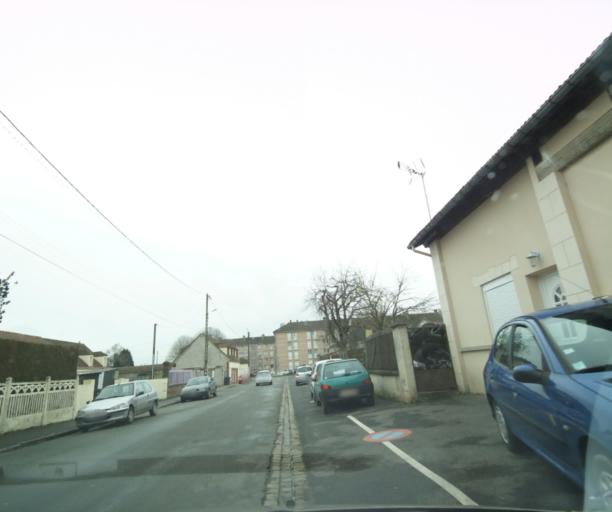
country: FR
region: Picardie
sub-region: Departement de l'Oise
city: Noyon
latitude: 49.5747
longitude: 3.0082
